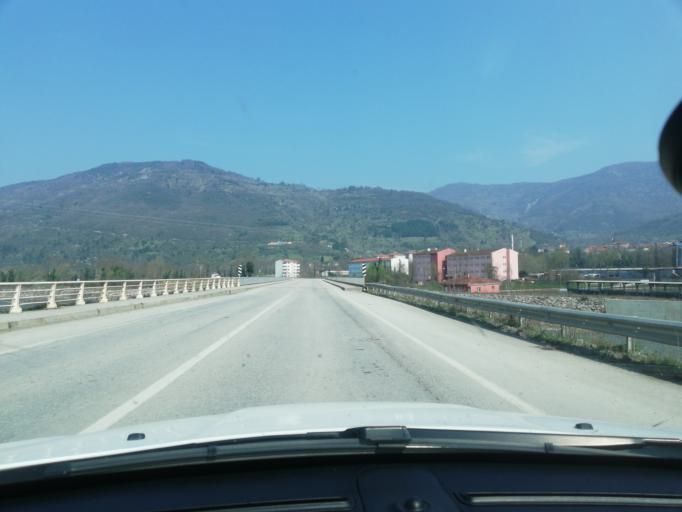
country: TR
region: Karabuk
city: Yenice
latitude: 41.2114
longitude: 32.3099
